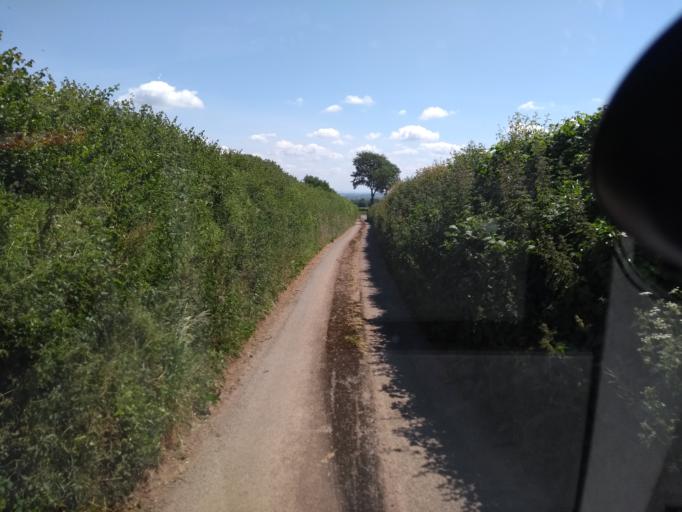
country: GB
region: England
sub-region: Somerset
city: North Petherton
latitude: 51.0660
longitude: -3.0279
